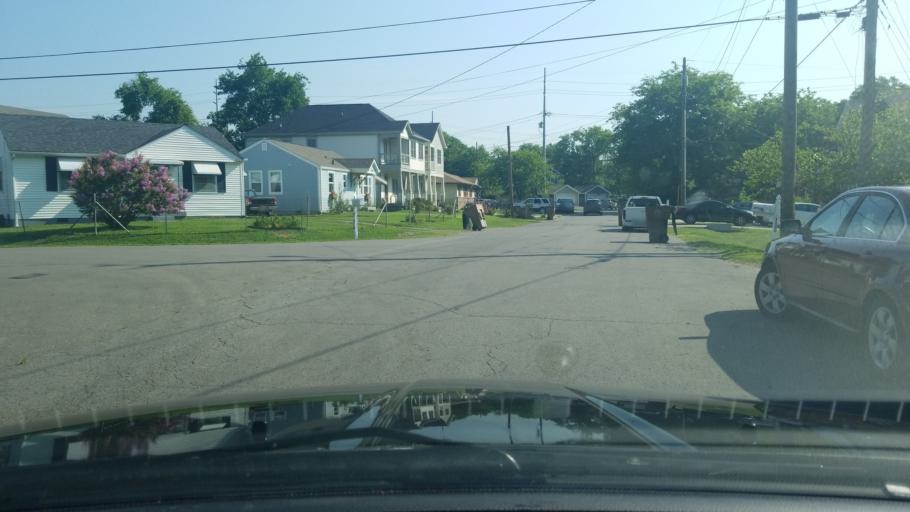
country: US
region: Tennessee
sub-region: Davidson County
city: Belle Meade
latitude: 36.1591
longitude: -86.8579
